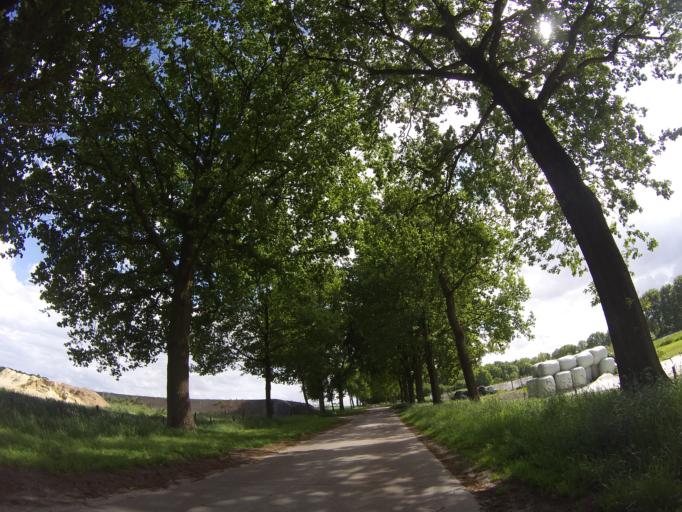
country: NL
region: Drenthe
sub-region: Gemeente Borger-Odoorn
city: Borger
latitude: 52.8822
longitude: 6.8698
